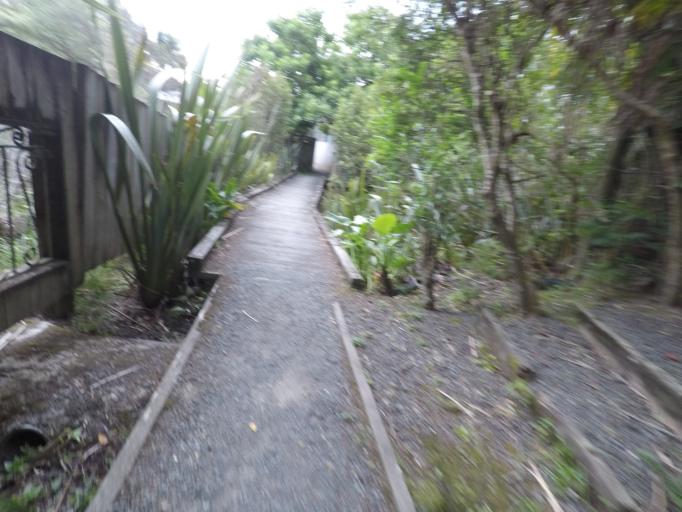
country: NZ
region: Northland
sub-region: Whangarei
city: Whangarei
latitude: -35.7174
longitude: 174.3289
